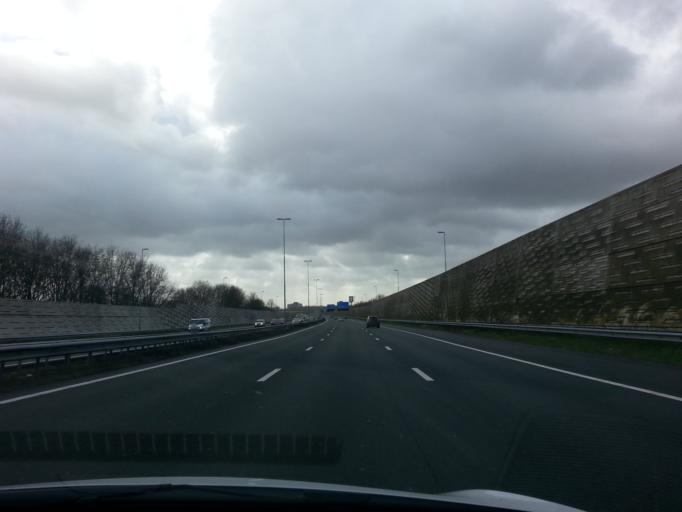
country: NL
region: North Brabant
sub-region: Gemeente 's-Hertogenbosch
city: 's-Hertogenbosch
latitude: 51.7353
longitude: 5.3083
